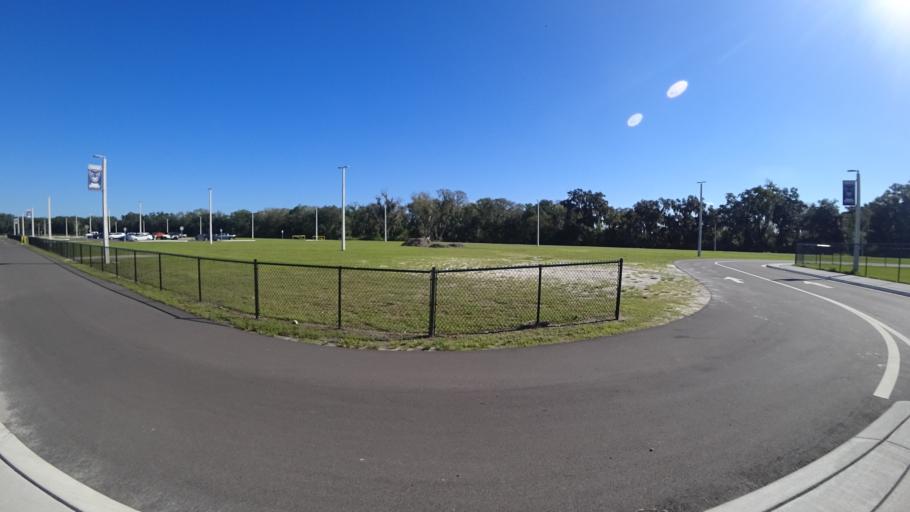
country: US
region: Florida
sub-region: Manatee County
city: Ellenton
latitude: 27.5806
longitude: -82.4382
